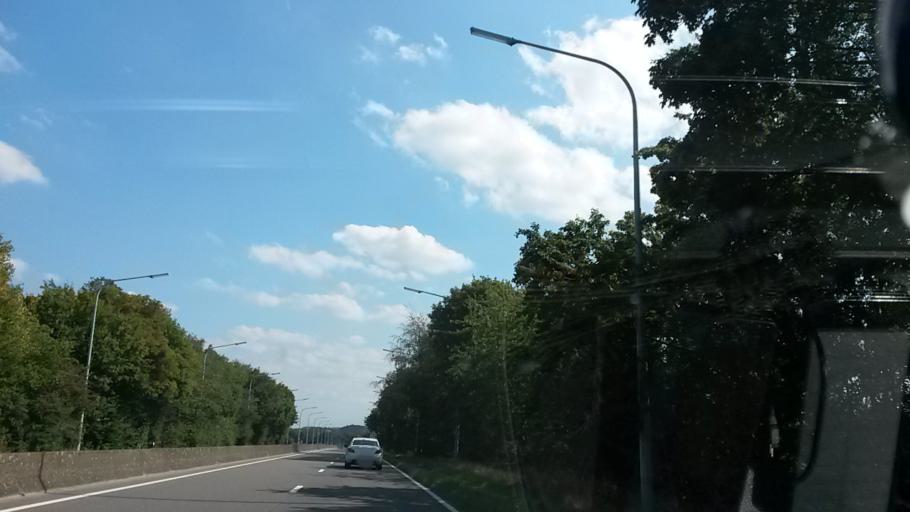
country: BE
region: Wallonia
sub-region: Province de Namur
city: Floreffe
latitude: 50.4273
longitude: 4.7228
